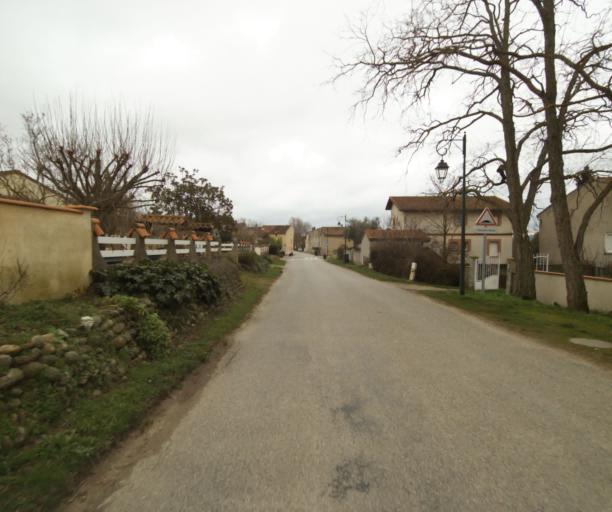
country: FR
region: Midi-Pyrenees
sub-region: Departement de l'Ariege
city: Pamiers
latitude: 43.1559
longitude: 1.6358
